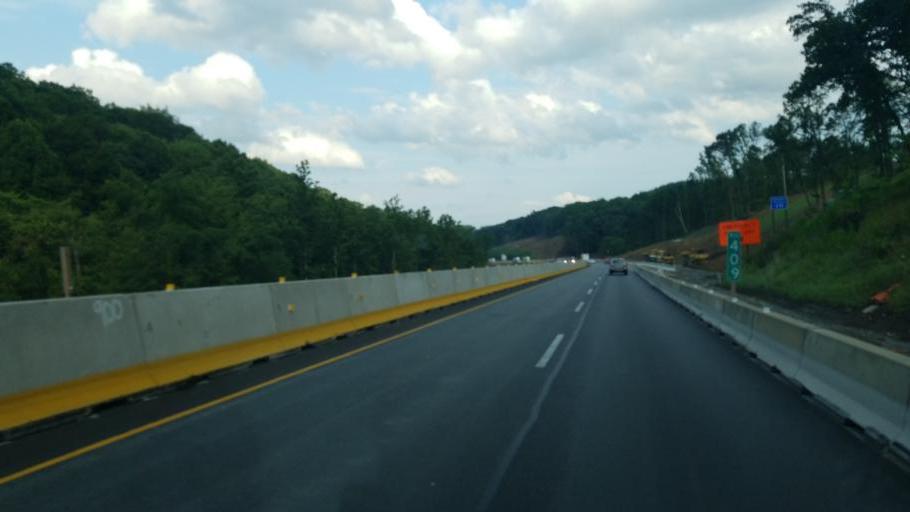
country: US
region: Pennsylvania
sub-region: Allegheny County
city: Allison Park
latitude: 40.5973
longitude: -79.9183
